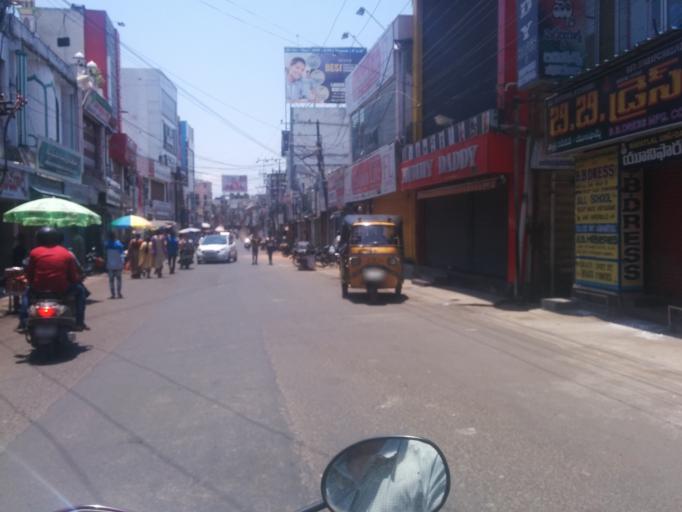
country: IN
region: Andhra Pradesh
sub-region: East Godavari
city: Rajahmundry
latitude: 17.0055
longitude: 81.7702
